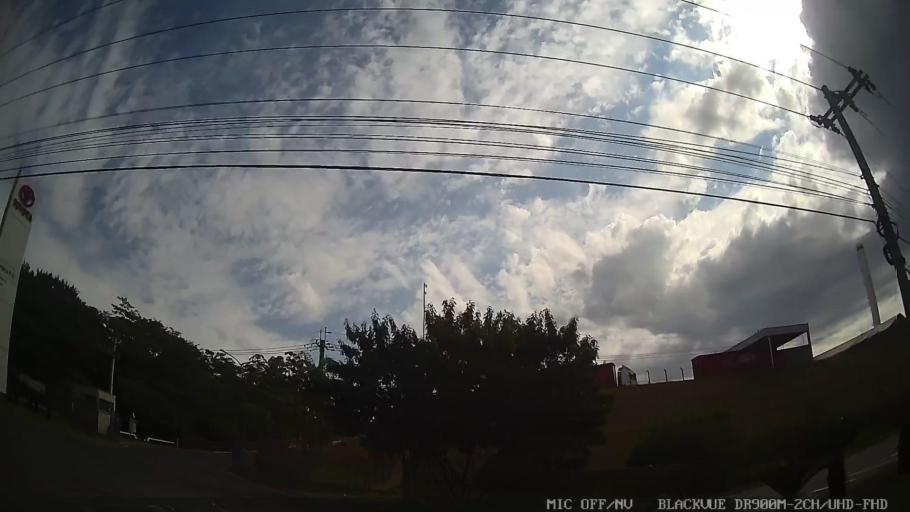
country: BR
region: Sao Paulo
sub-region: Indaiatuba
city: Indaiatuba
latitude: -23.1416
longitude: -47.2481
